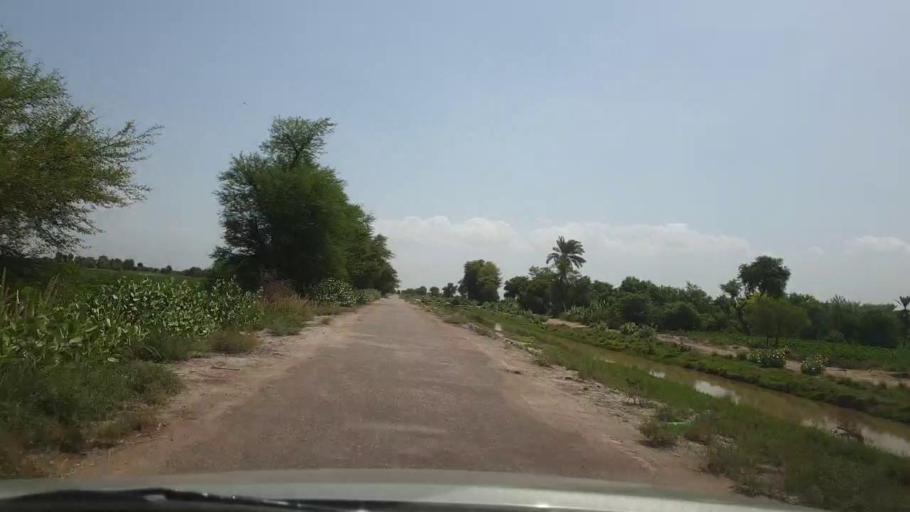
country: PK
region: Sindh
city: Pano Aqil
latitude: 27.7267
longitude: 69.0901
